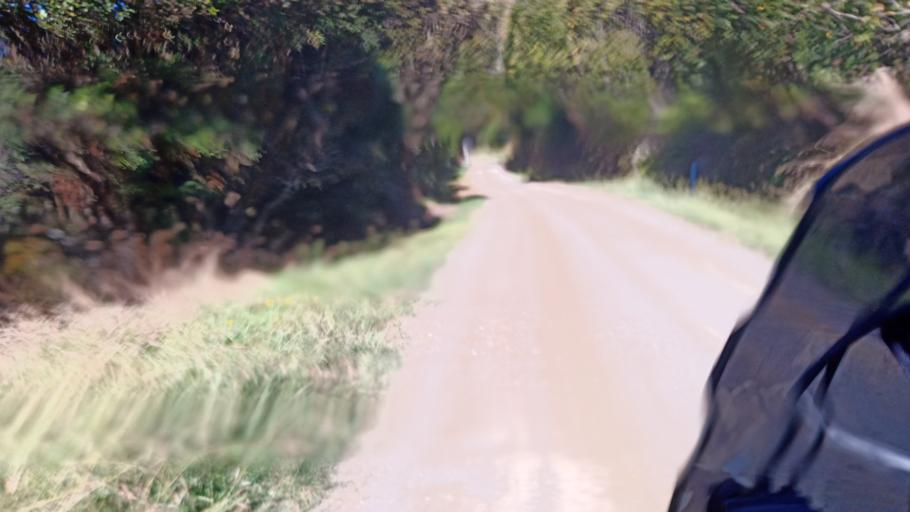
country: NZ
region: Bay of Plenty
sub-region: Opotiki District
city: Opotiki
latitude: -38.2481
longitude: 177.5941
